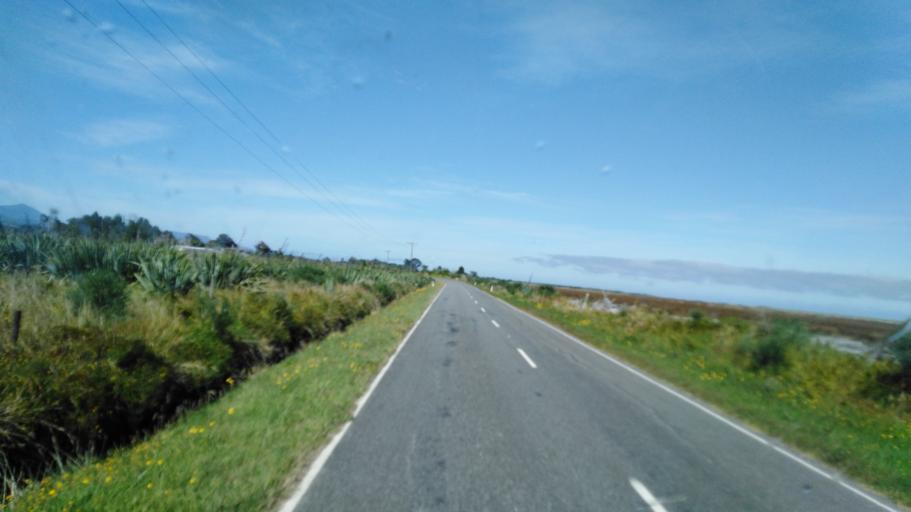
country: NZ
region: West Coast
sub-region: Buller District
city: Westport
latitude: -41.2818
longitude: 172.1062
